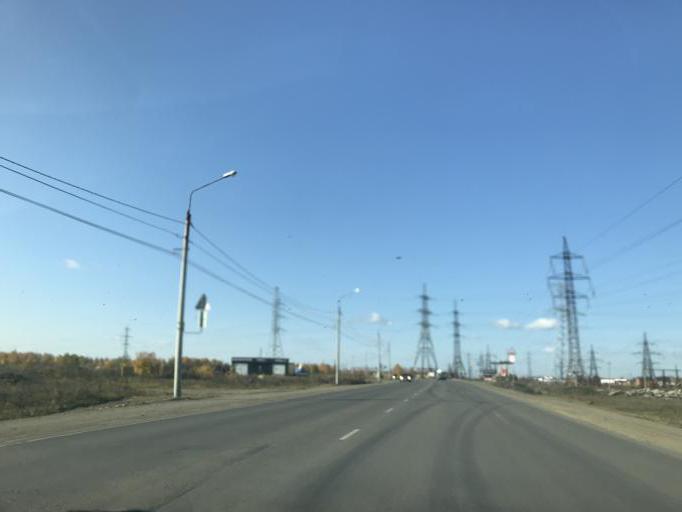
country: RU
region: Chelyabinsk
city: Roshchino
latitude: 55.2237
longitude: 61.2926
